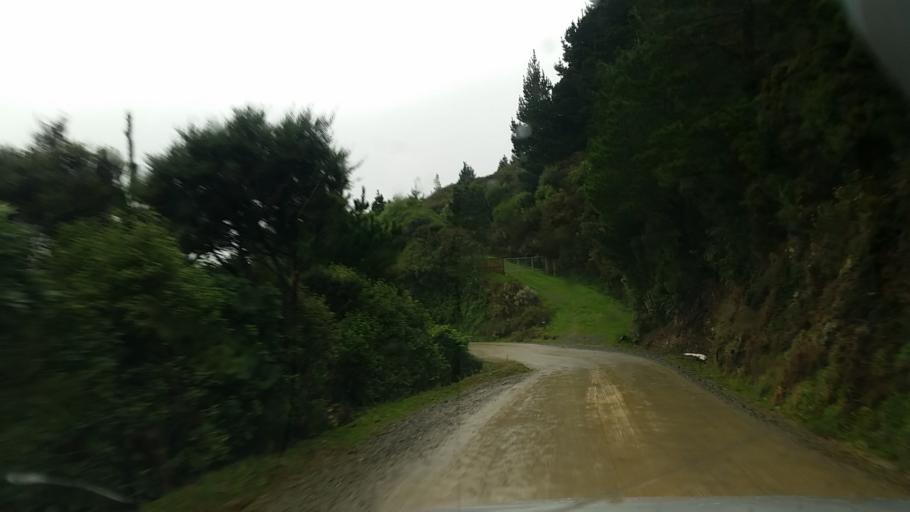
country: NZ
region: Marlborough
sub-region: Marlborough District
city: Picton
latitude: -41.1740
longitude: 174.0403
